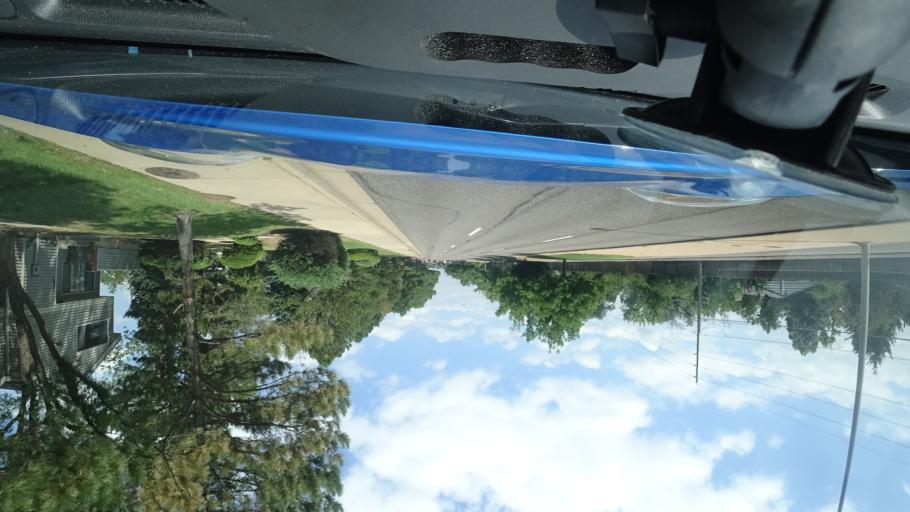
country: US
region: Colorado
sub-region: Adams County
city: Aurora
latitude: 39.7113
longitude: -104.8513
